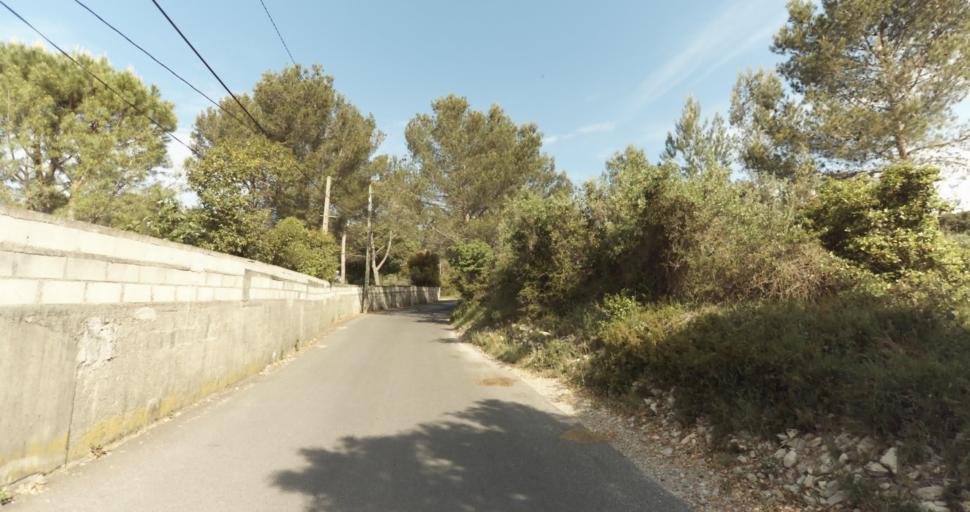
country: FR
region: Languedoc-Roussillon
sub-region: Departement du Gard
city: Poulx
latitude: 43.8697
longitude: 4.3950
